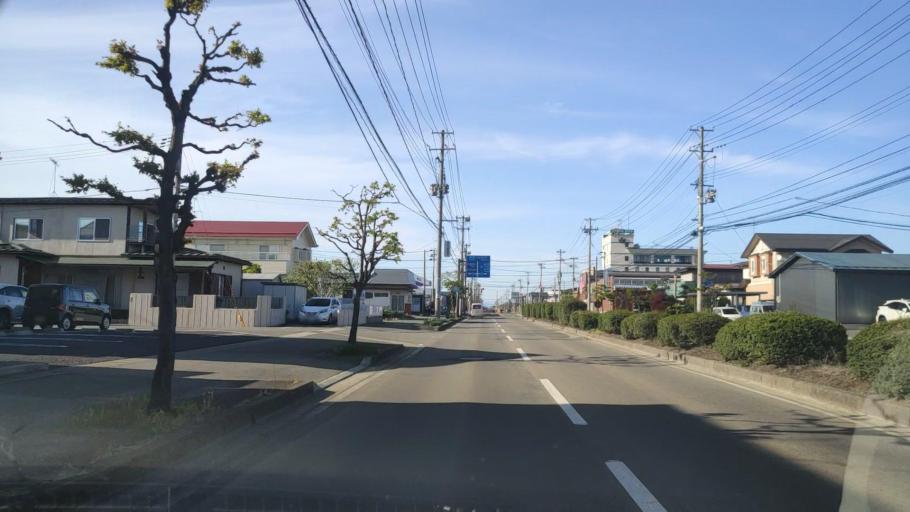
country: JP
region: Yamagata
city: Tendo
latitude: 38.3645
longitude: 140.3668
